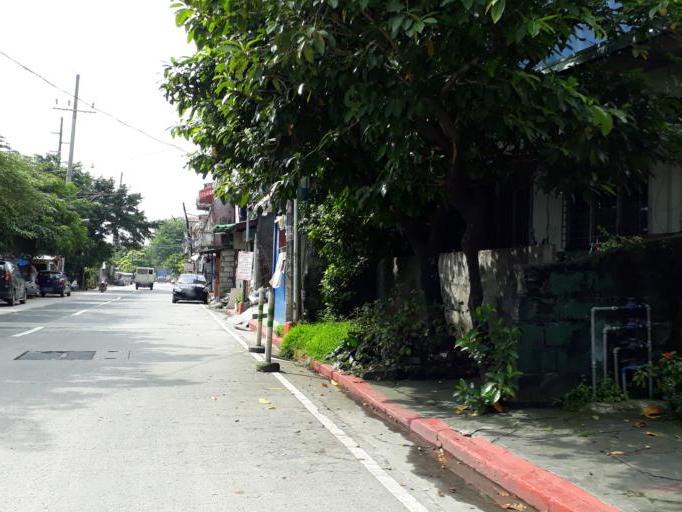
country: PH
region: Metro Manila
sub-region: City of Manila
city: Manila
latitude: 14.6078
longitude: 121.0013
